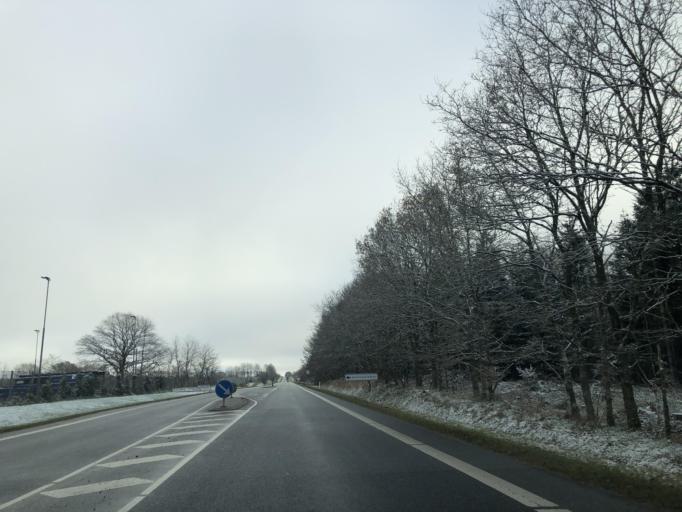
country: DK
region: Central Jutland
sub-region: Hedensted Kommune
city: Torring
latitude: 55.9589
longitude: 9.4103
